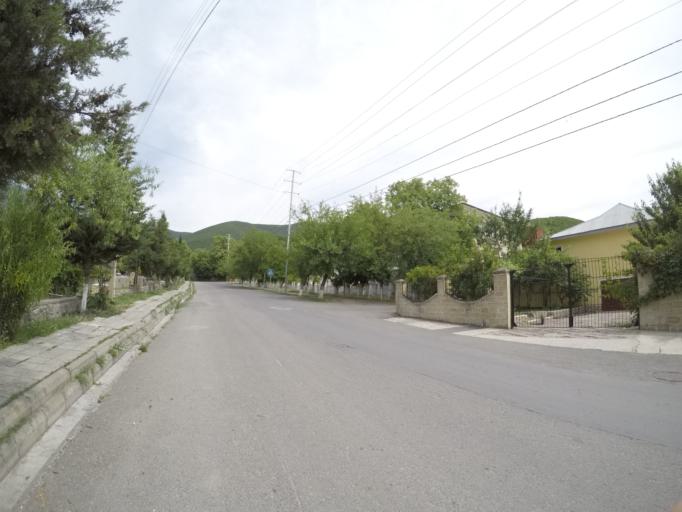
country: AZ
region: Shaki City
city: Sheki
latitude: 41.2002
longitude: 47.1872
